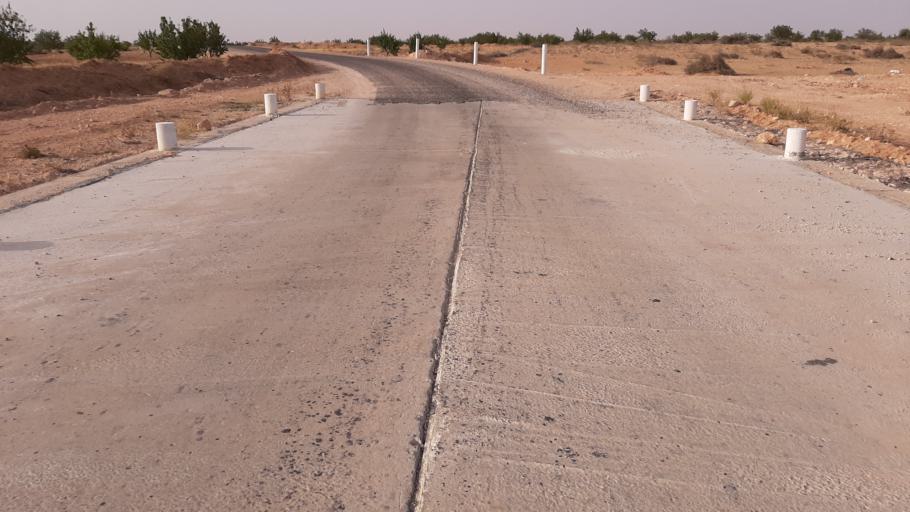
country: TN
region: Safaqis
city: Bi'r `Ali Bin Khalifah
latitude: 34.5284
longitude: 10.1985
